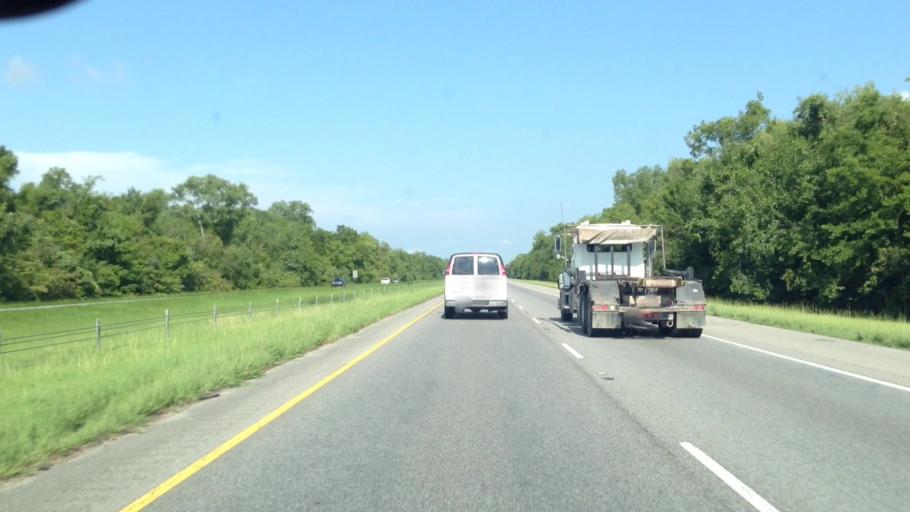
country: US
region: Louisiana
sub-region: Saint John the Baptist Parish
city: Reserve
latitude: 30.1131
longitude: -90.5660
